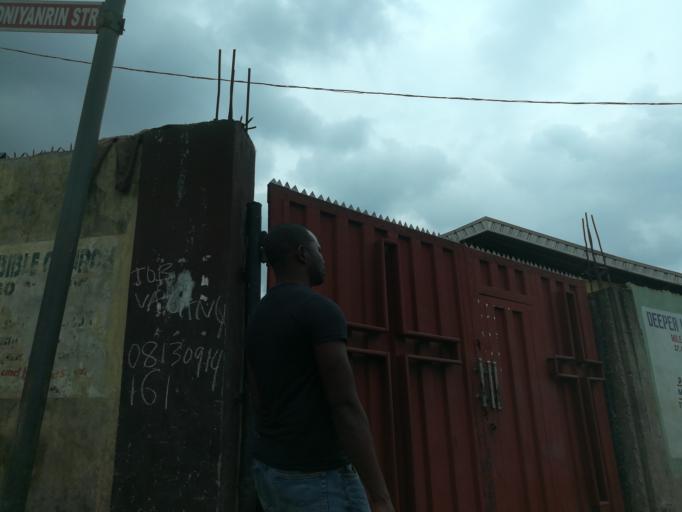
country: NG
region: Lagos
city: Ojota
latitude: 6.6114
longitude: 3.3980
